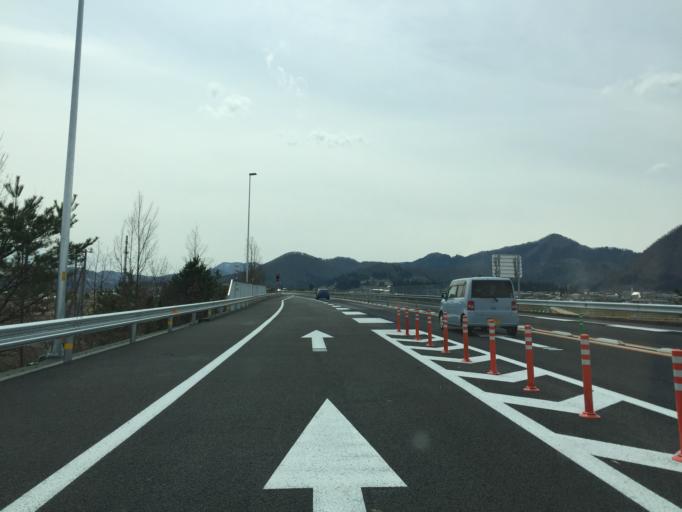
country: JP
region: Yamagata
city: Yamagata-shi
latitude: 38.2445
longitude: 140.2778
